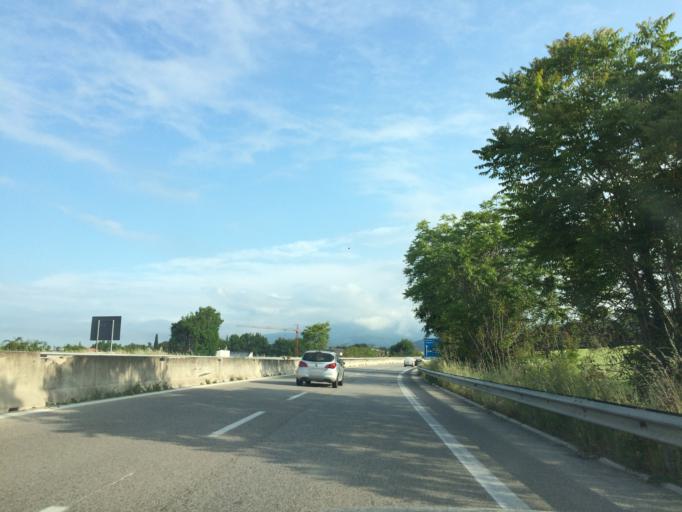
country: IT
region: Umbria
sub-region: Provincia di Perugia
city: Foligno
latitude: 42.9380
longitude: 12.7229
